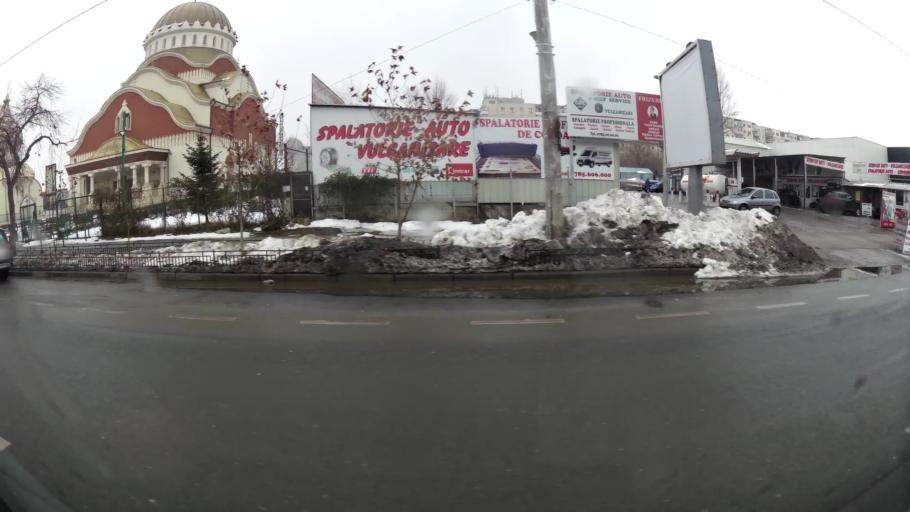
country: RO
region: Ilfov
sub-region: Comuna Chiajna
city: Rosu
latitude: 44.4203
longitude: 26.0346
